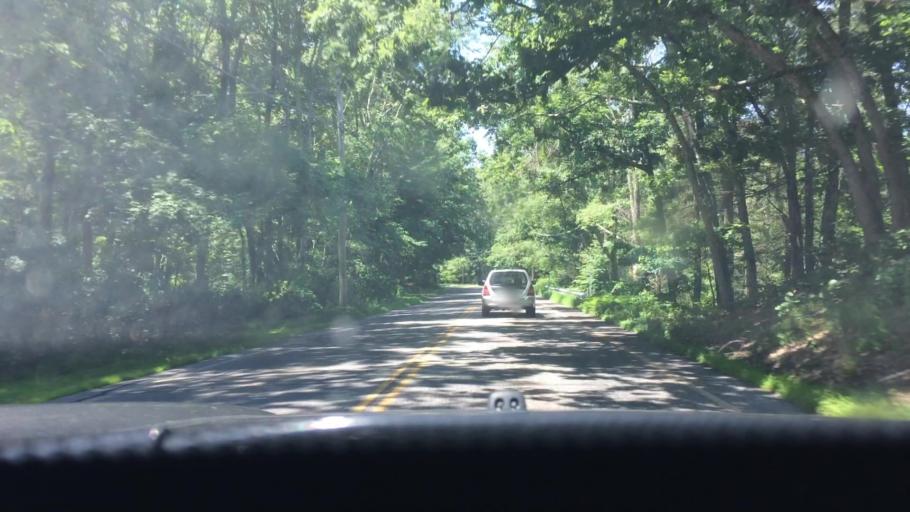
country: US
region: Rhode Island
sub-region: Providence County
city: Harrisville
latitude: 42.0218
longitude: -71.6692
